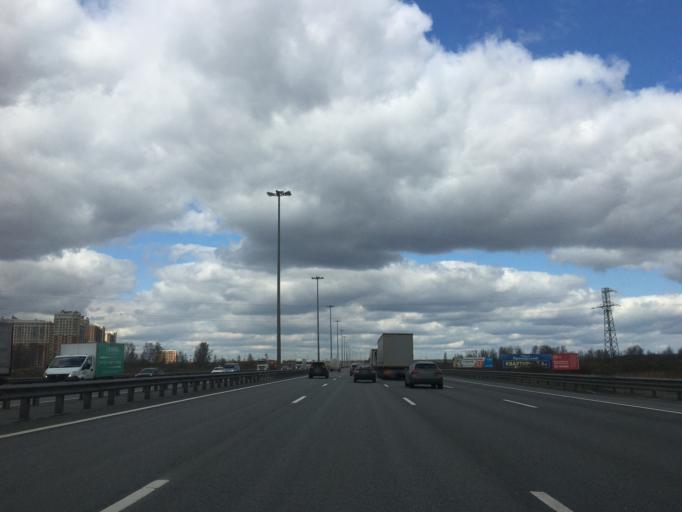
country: RU
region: Leningrad
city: Rybatskoye
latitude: 59.9094
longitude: 30.5261
